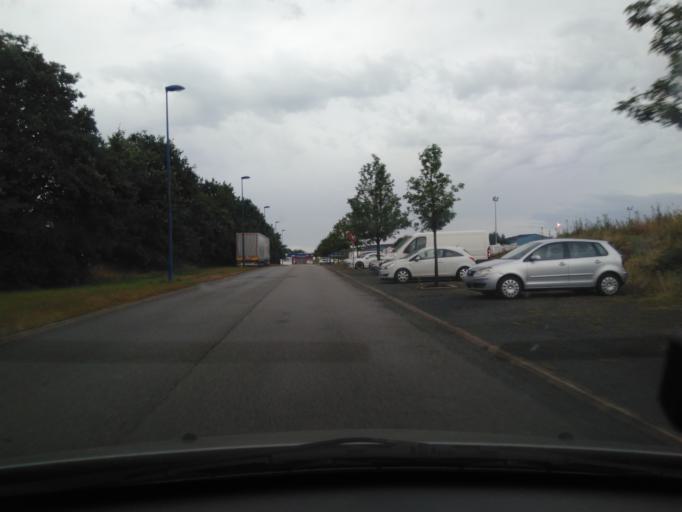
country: FR
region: Pays de la Loire
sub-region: Departement de la Vendee
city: Mouilleron-le-Captif
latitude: 46.7437
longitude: -1.4263
